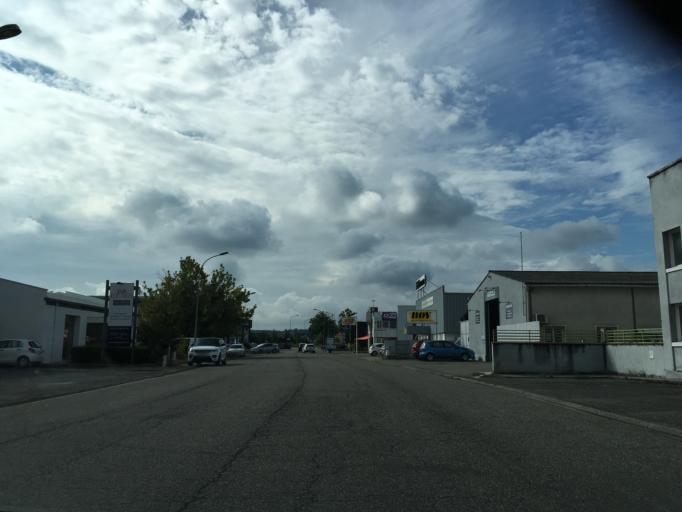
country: FR
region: Aquitaine
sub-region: Departement du Lot-et-Garonne
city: Agen
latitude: 44.1805
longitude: 0.6302
